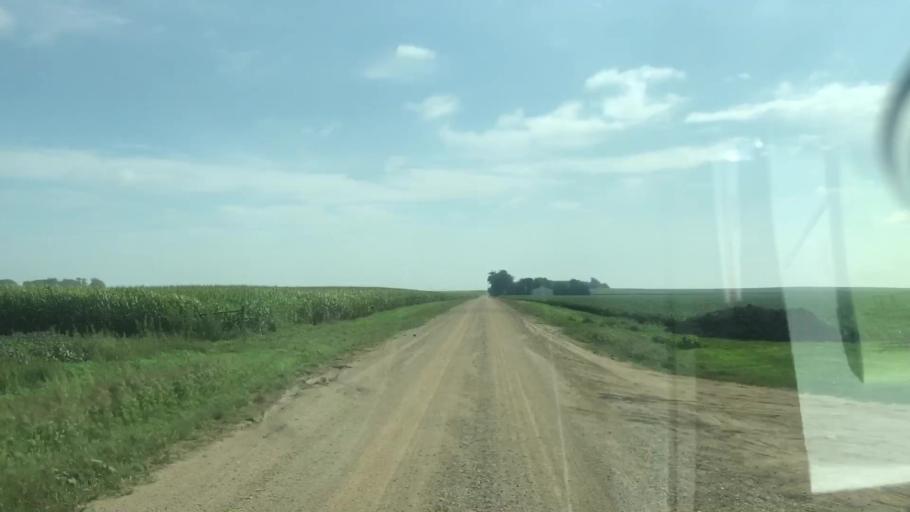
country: US
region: Iowa
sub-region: O'Brien County
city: Sheldon
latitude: 43.2153
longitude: -95.9520
